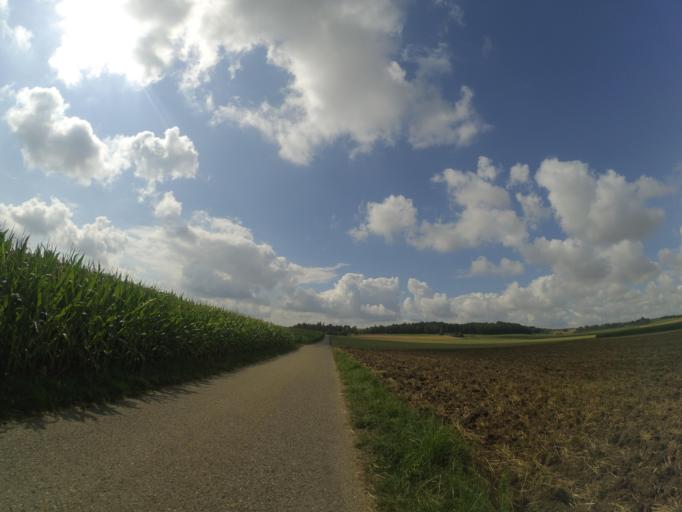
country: DE
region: Baden-Wuerttemberg
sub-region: Tuebingen Region
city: Bernstadt
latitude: 48.4926
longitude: 10.0159
